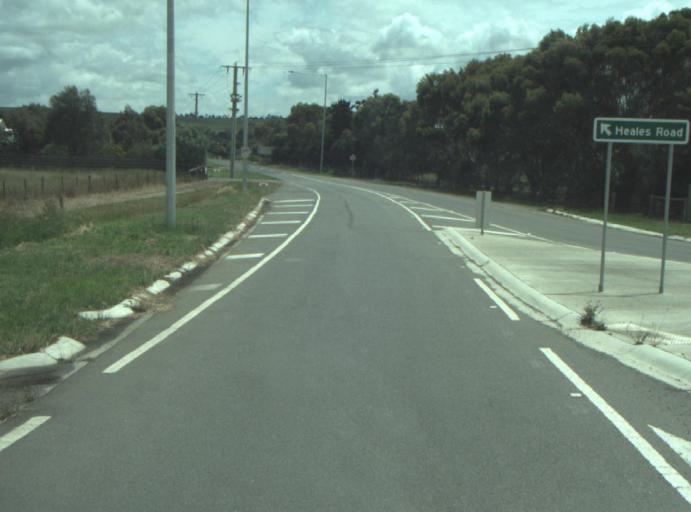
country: AU
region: Victoria
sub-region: Greater Geelong
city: Lara
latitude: -38.0481
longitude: 144.3577
